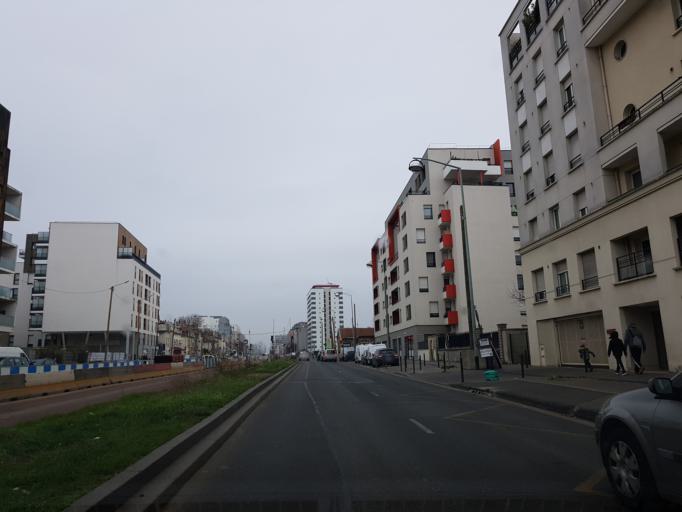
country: FR
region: Ile-de-France
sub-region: Departement du Val-de-Marne
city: Ivry-sur-Seine
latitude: 48.7952
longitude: 2.3843
